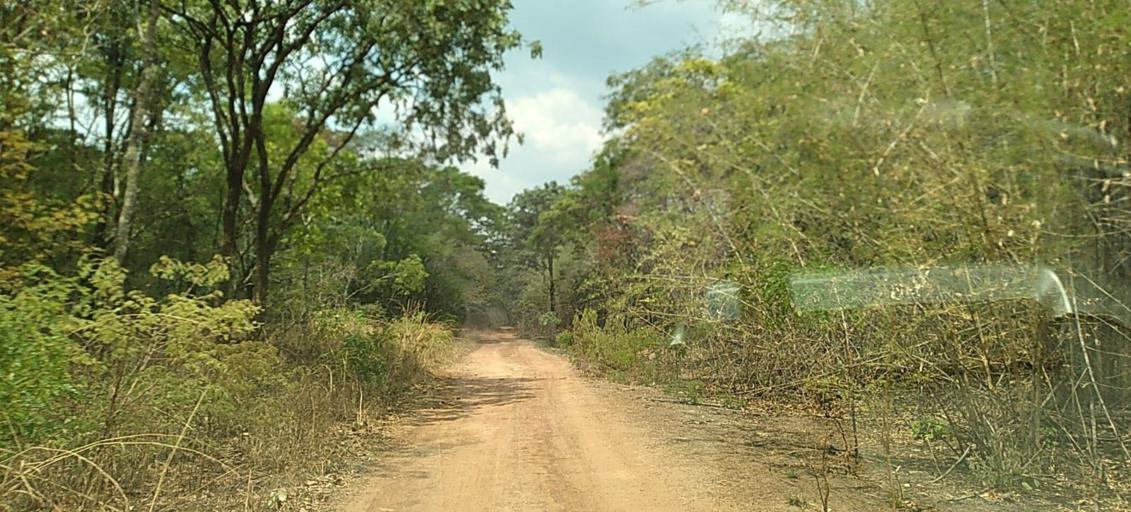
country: ZM
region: Copperbelt
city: Chingola
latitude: -12.7693
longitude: 27.6999
